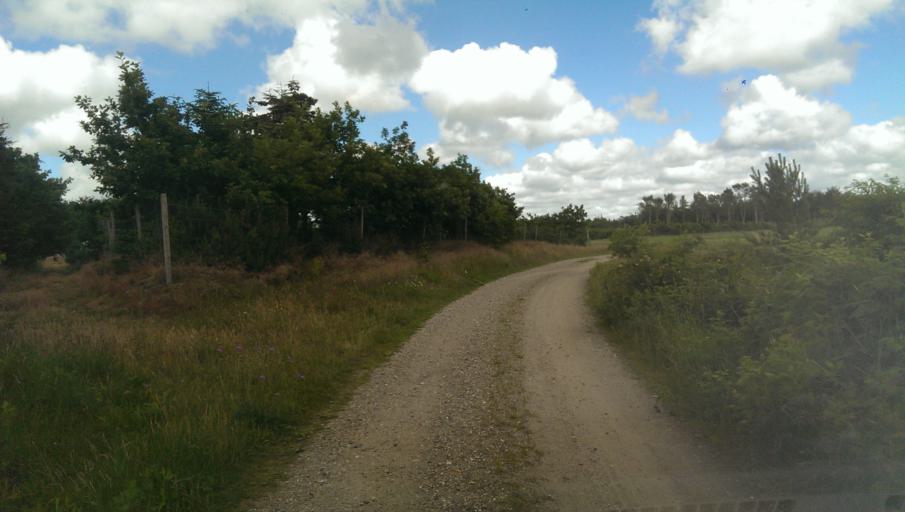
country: DK
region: Central Jutland
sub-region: Holstebro Kommune
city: Ulfborg
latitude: 56.2644
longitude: 8.2488
